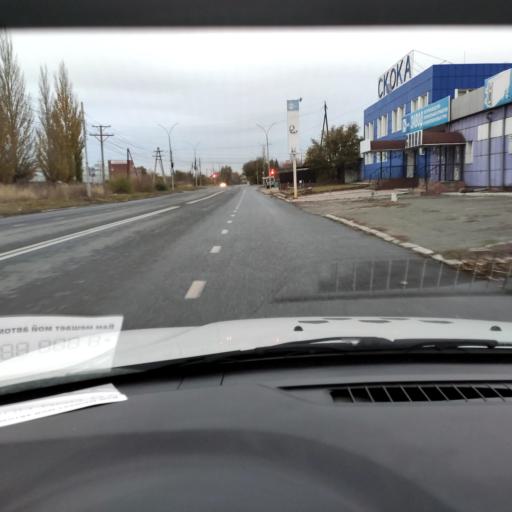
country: RU
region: Samara
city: Tol'yatti
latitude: 53.5590
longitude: 49.2948
